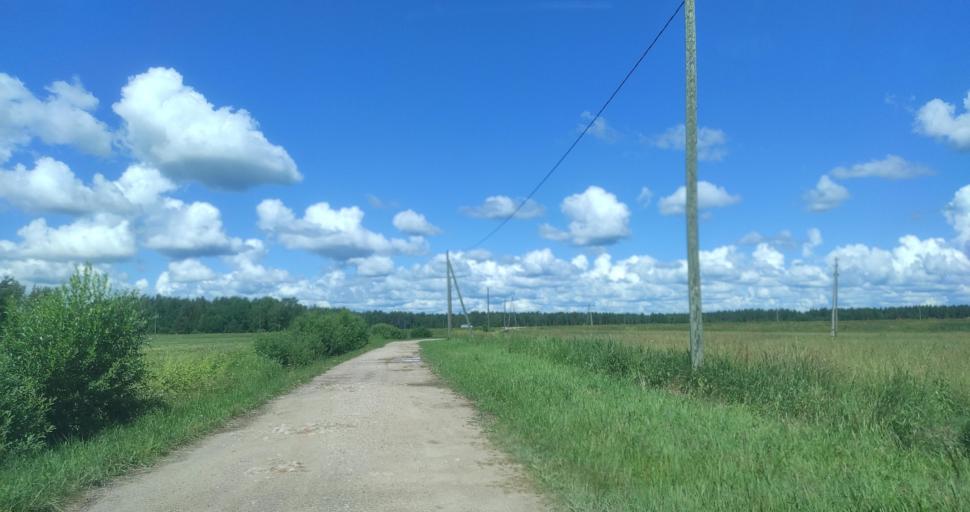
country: LV
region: Kuldigas Rajons
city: Kuldiga
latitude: 56.9945
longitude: 22.1251
